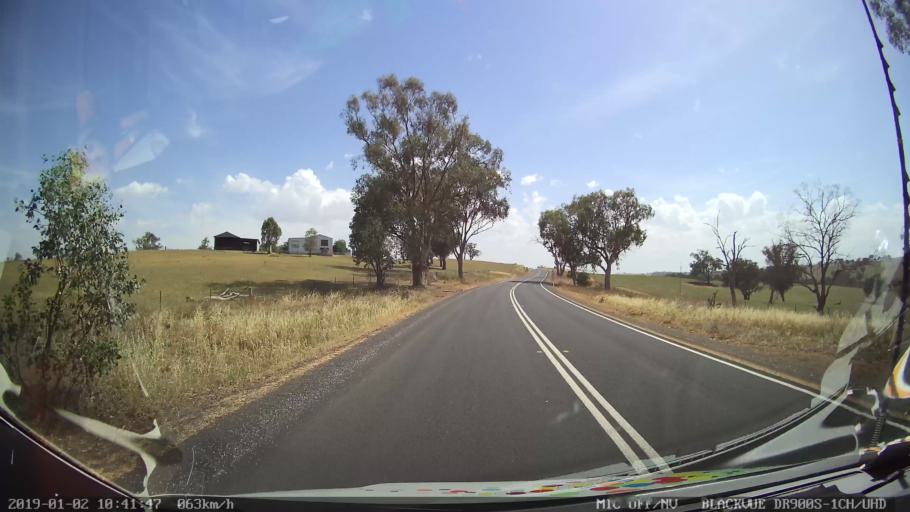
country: AU
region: New South Wales
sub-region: Cootamundra
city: Cootamundra
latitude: -34.7911
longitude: 148.3070
